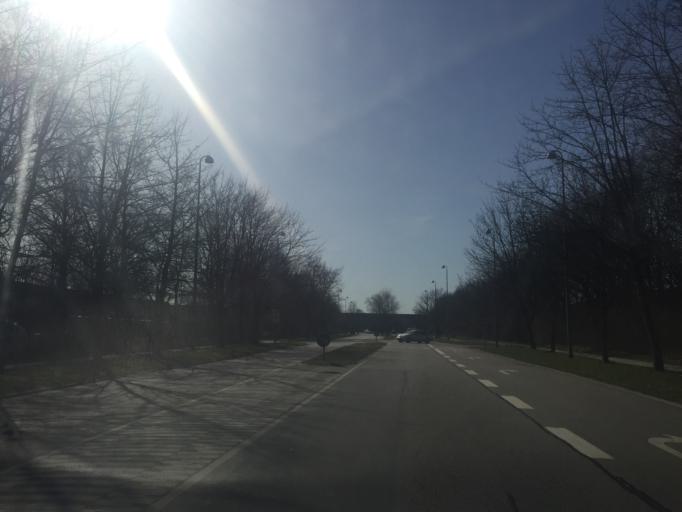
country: DK
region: Capital Region
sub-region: Glostrup Kommune
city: Glostrup
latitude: 55.6808
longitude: 12.4135
